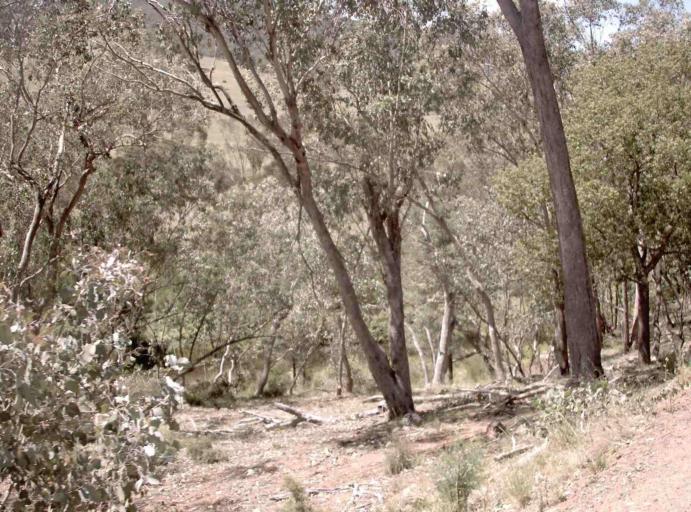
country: AU
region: New South Wales
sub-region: Snowy River
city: Jindabyne
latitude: -37.0871
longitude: 148.4439
